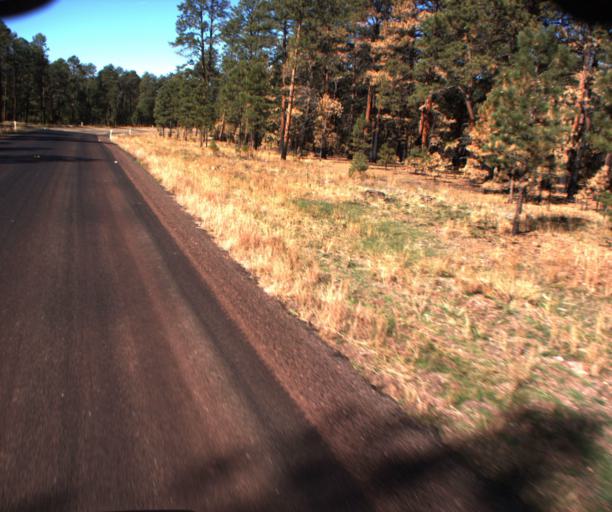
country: US
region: Arizona
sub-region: Coconino County
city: Fredonia
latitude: 36.7490
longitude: -112.2645
